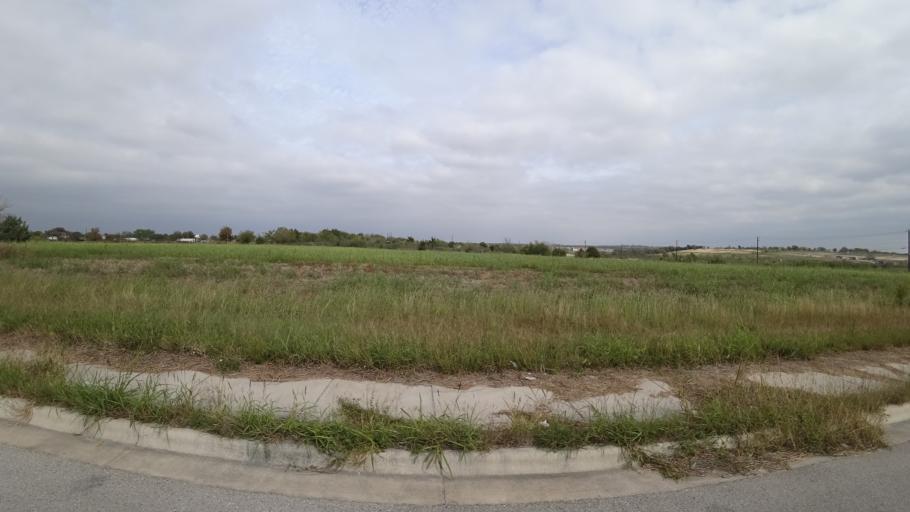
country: US
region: Texas
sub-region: Travis County
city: Pflugerville
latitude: 30.3786
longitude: -97.6093
